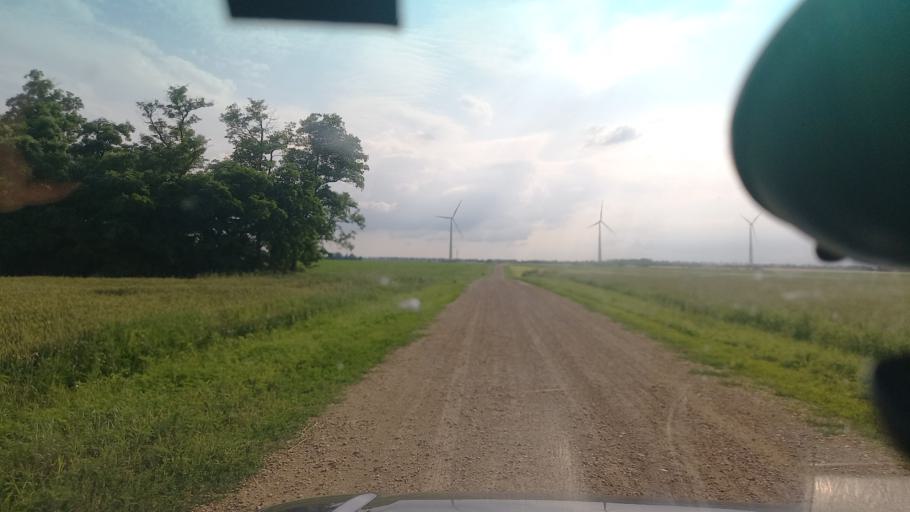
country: RU
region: Adygeya
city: Giaginskaya
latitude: 44.9538
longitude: 40.0914
